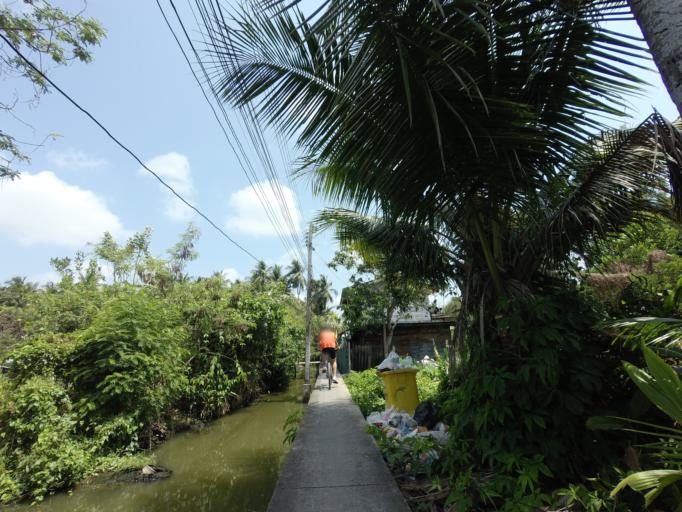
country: TH
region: Bangkok
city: Chom Thong
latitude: 13.6567
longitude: 100.4909
